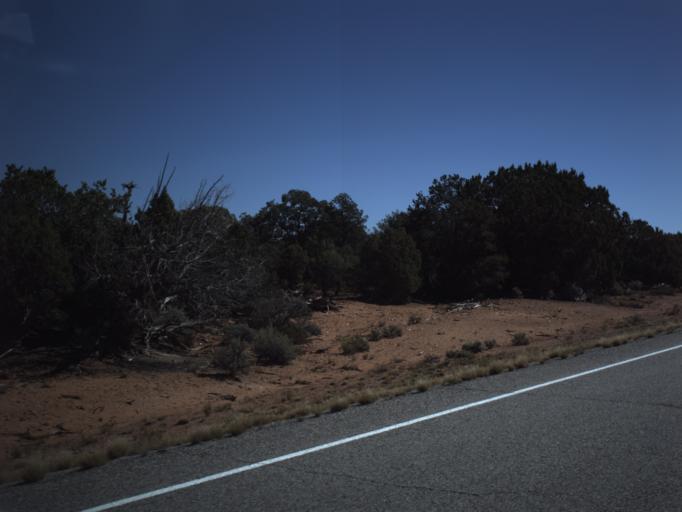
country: US
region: Utah
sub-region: San Juan County
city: Blanding
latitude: 37.5598
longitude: -110.0066
